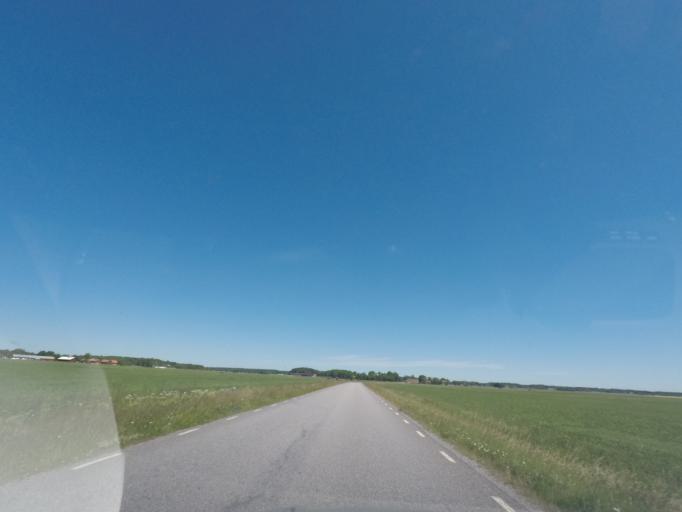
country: SE
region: Uppsala
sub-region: Enkopings Kommun
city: Irsta
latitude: 59.6889
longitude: 16.9632
